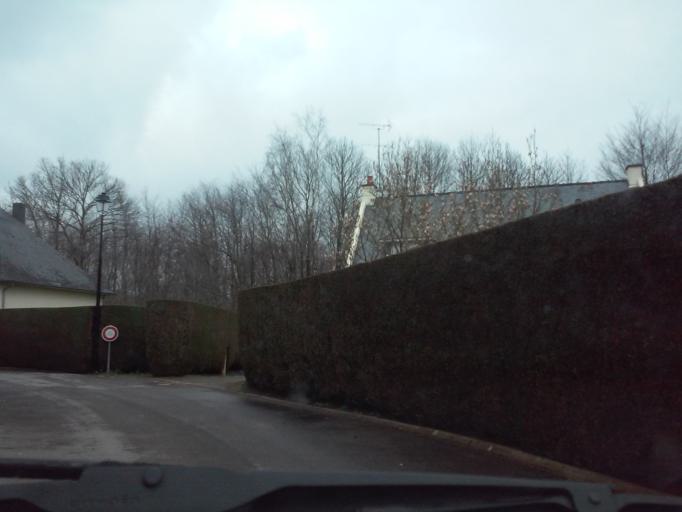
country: FR
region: Brittany
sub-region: Departement d'Ille-et-Vilaine
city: Fougeres
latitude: 48.3692
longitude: -1.1769
